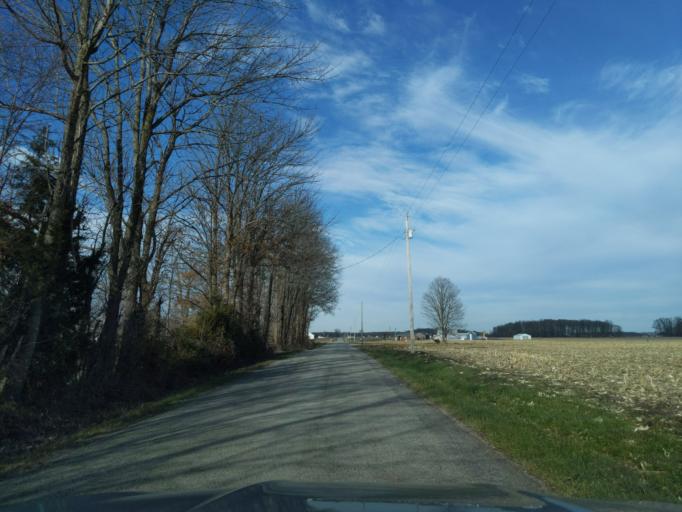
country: US
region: Indiana
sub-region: Decatur County
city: Greensburg
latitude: 39.2407
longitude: -85.4196
